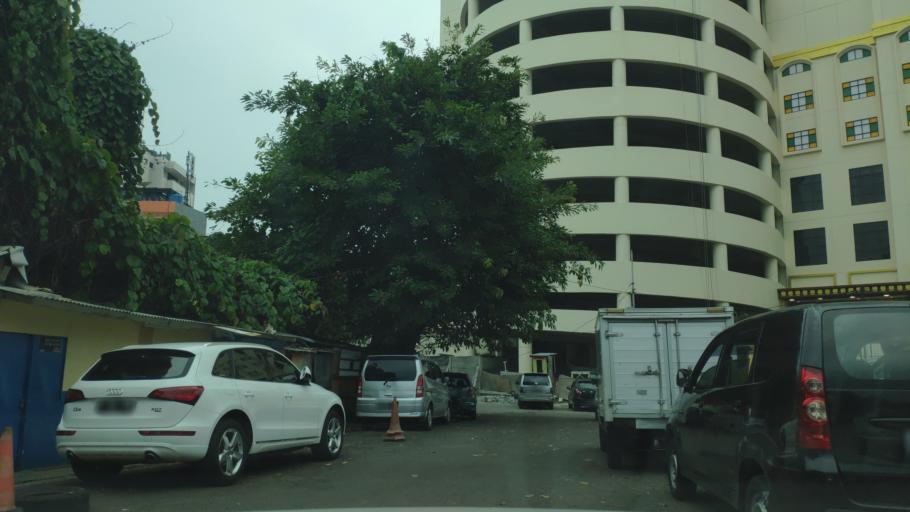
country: ID
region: Jakarta Raya
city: Jakarta
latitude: -6.1401
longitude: 106.8135
